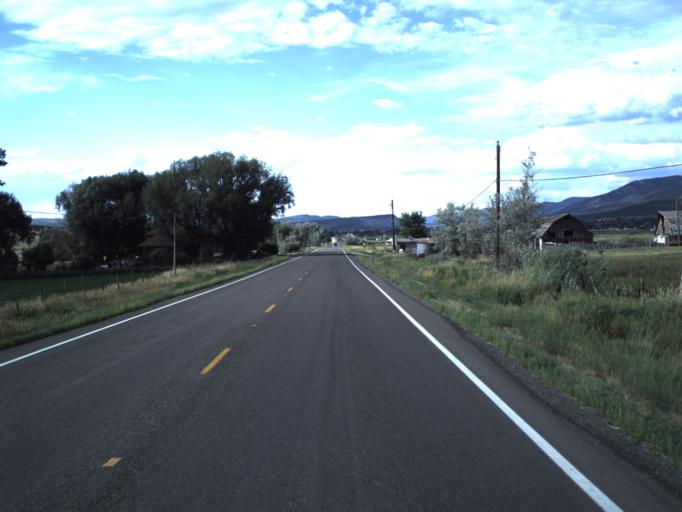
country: US
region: Utah
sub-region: Sanpete County
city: Fairview
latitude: 39.6000
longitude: -111.4447
